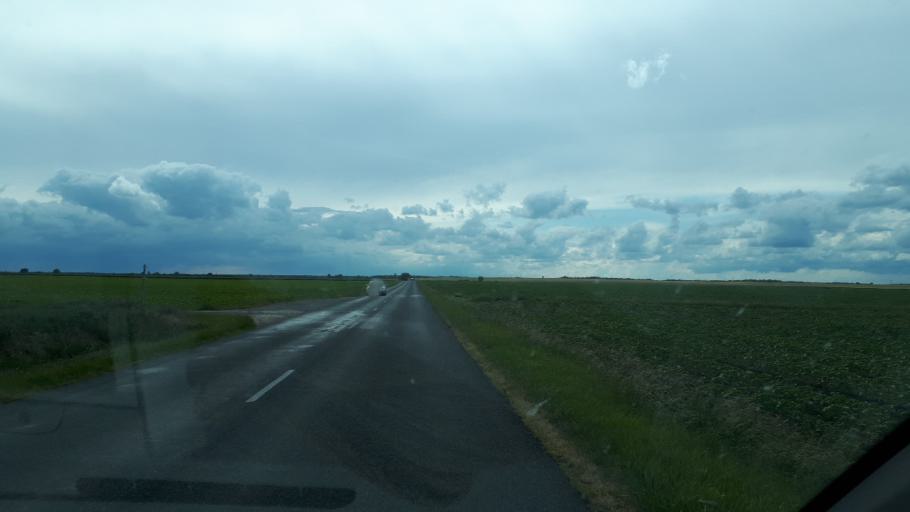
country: FR
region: Centre
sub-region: Departement du Cher
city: Marmagne
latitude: 47.0812
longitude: 2.2369
